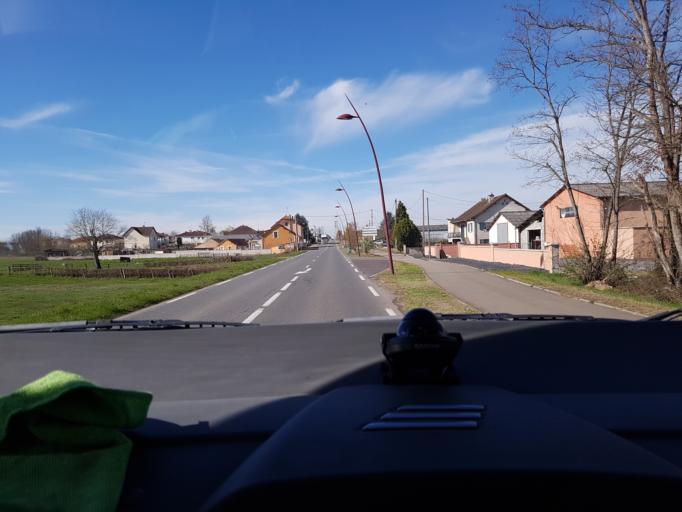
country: FR
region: Bourgogne
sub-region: Departement de Saone-et-Loire
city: Digoin
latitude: 46.4961
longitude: 4.0066
